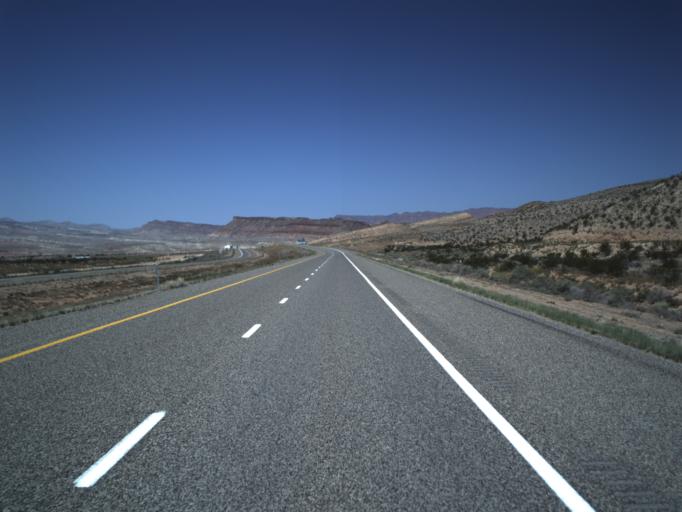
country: US
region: Utah
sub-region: Washington County
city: Saint George
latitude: 37.0124
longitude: -113.5916
